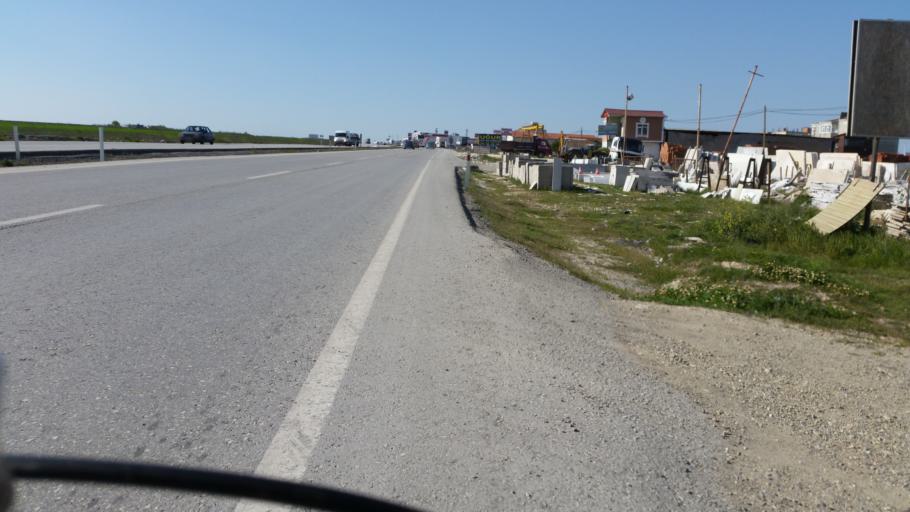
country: TR
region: Tekirdag
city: Cerkezkoey
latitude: 41.3380
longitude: 27.9668
